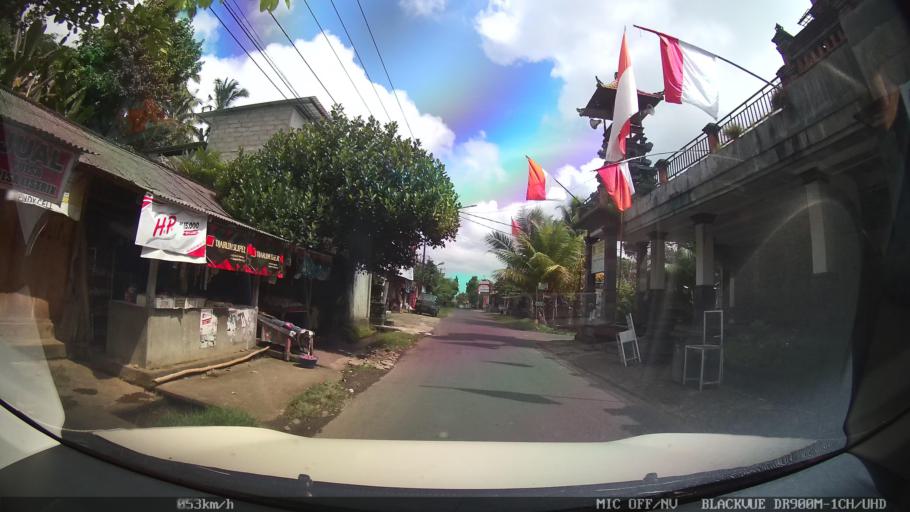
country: ID
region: Bali
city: Banjar Madangan Kaja
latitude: -8.4747
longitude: 115.3241
